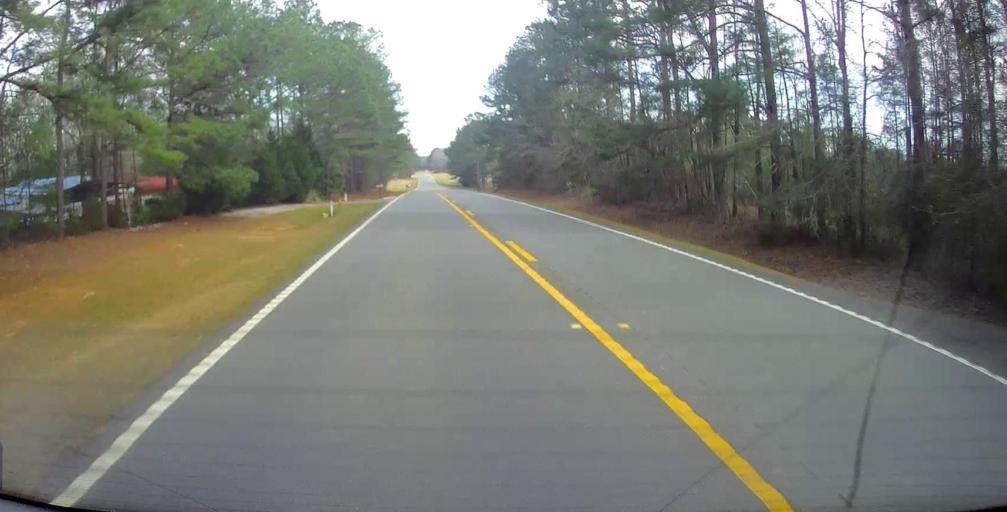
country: US
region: Georgia
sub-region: Harris County
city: Hamilton
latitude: 32.7020
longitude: -84.8169
